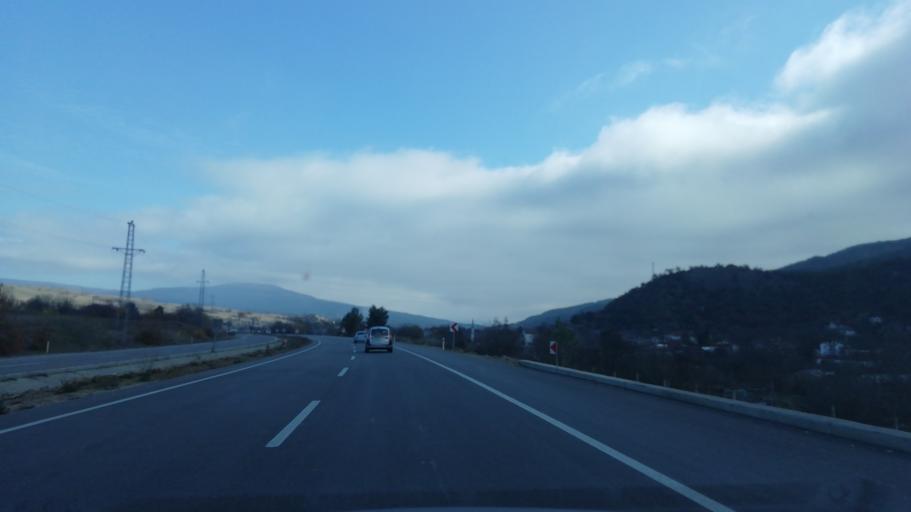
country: TR
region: Karabuk
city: Safranbolu
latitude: 41.2167
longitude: 32.7346
